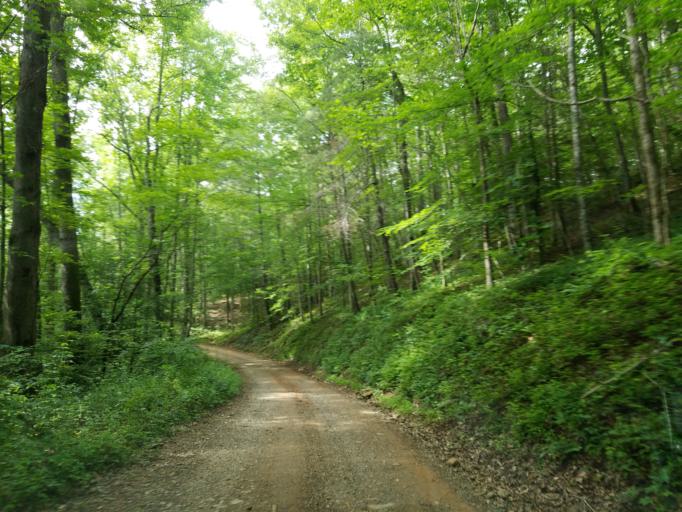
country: US
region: Georgia
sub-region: Union County
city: Blairsville
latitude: 34.7332
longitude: -84.0594
